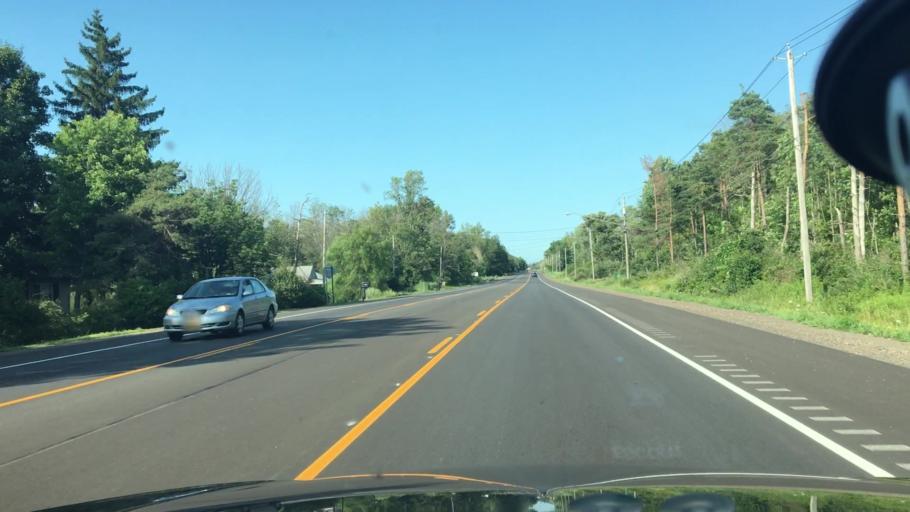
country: US
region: New York
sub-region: Erie County
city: Wanakah
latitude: 42.7132
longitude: -78.9108
